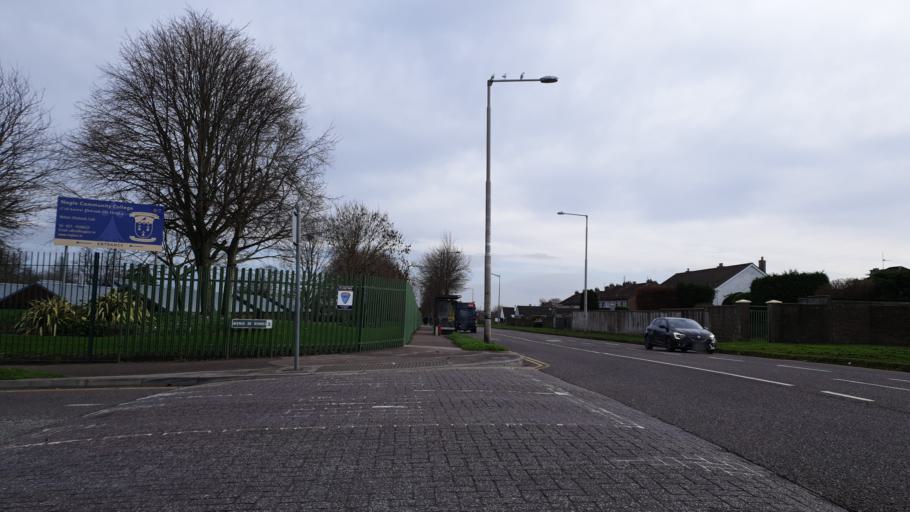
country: IE
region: Munster
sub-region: County Cork
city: Passage West
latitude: 51.8908
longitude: -8.4043
